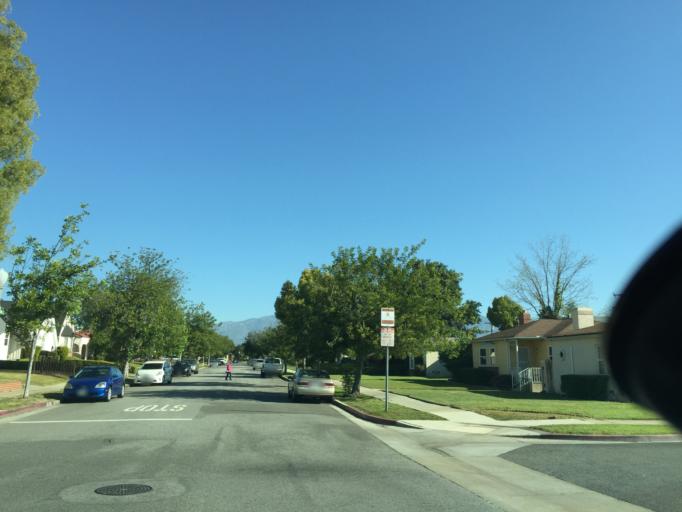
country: US
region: California
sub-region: Los Angeles County
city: Alhambra
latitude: 34.0806
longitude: -118.1243
